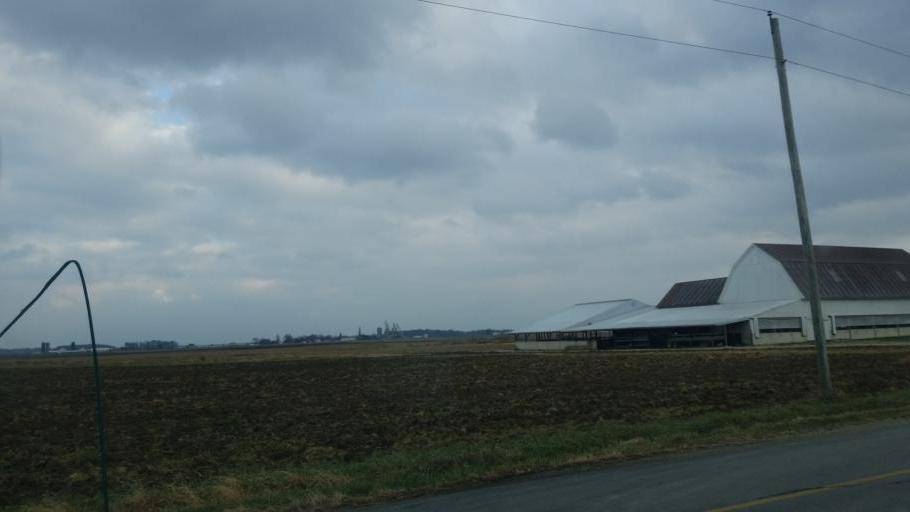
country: US
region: Ohio
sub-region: Mercer County
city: Fort Recovery
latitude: 40.5136
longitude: -84.8028
